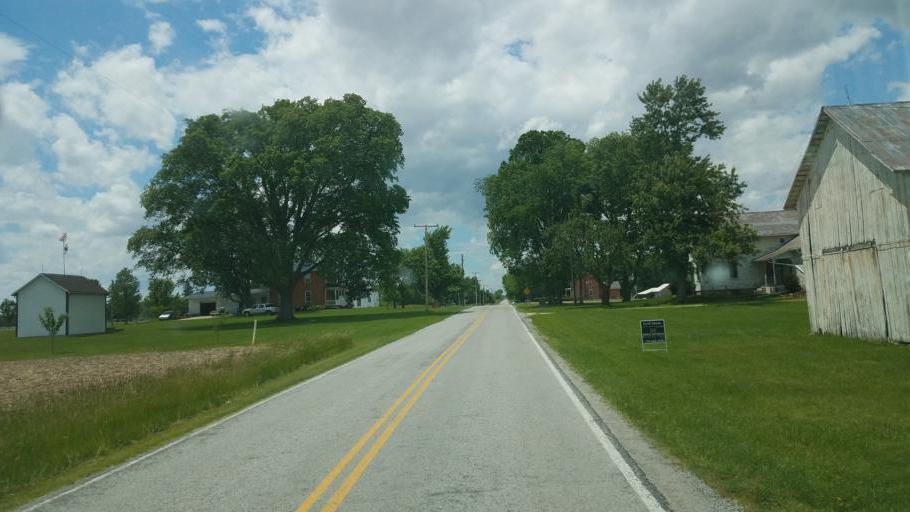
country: US
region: Ohio
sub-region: Huron County
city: Monroeville
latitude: 41.1649
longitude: -82.7880
